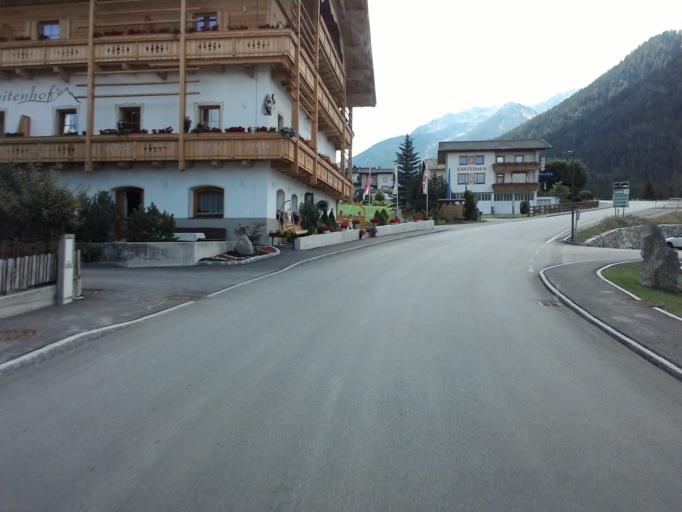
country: AT
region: Tyrol
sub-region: Politischer Bezirk Lienz
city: Kartitsch
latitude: 46.7260
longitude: 12.4989
